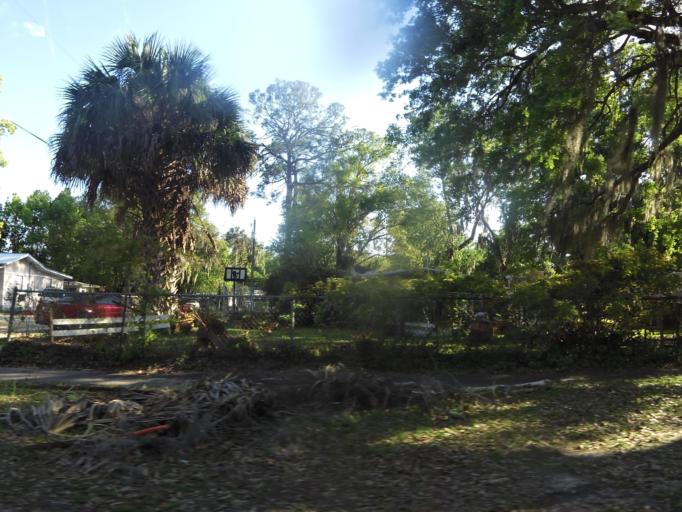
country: US
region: Florida
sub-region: Putnam County
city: Palatka
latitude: 29.6474
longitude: -81.6438
